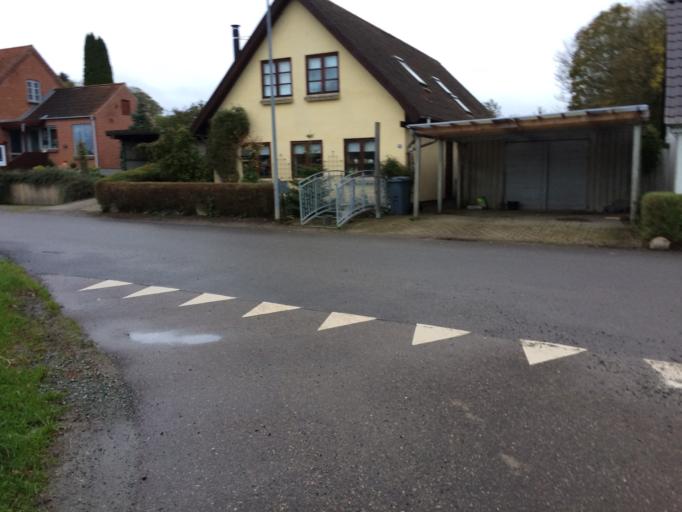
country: DK
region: South Denmark
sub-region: Vejle Kommune
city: Borkop
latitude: 55.6087
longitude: 9.6471
